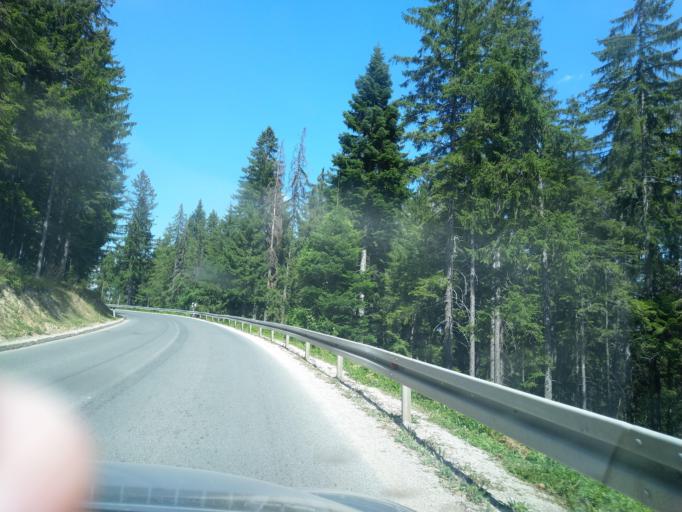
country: RS
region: Central Serbia
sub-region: Zlatiborski Okrug
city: Nova Varos
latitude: 43.4442
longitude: 19.8209
